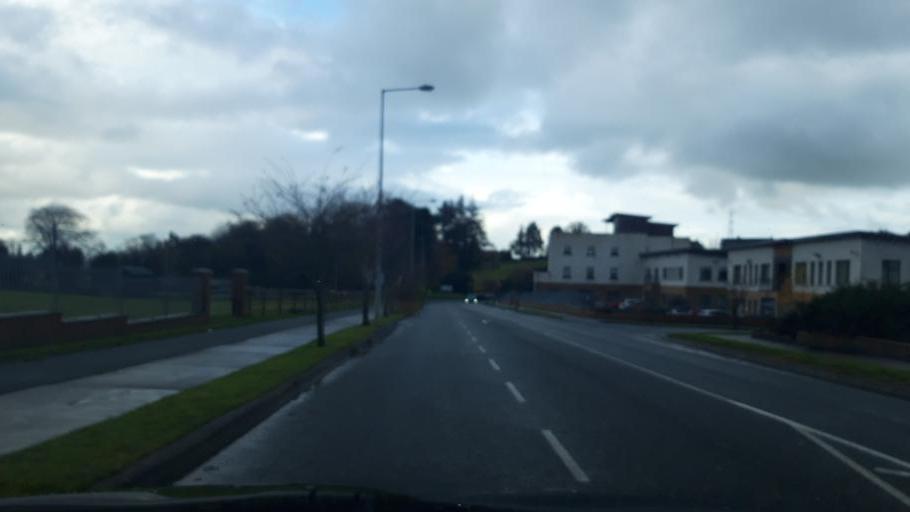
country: IE
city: Newtownmountkennedy
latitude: 53.0854
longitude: -6.1077
